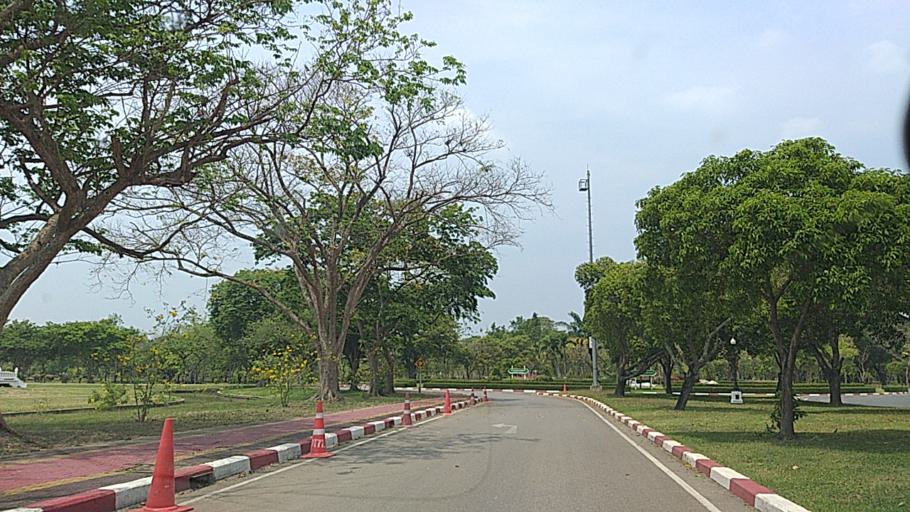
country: TH
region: Bangkok
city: Thawi Watthana
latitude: 13.7788
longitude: 100.3263
